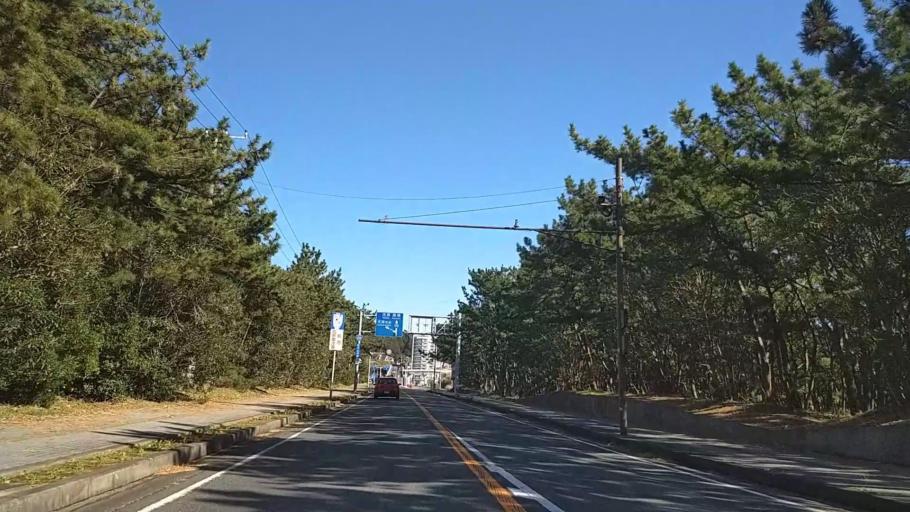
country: JP
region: Chiba
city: Kawaguchi
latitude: 35.1205
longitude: 140.1287
